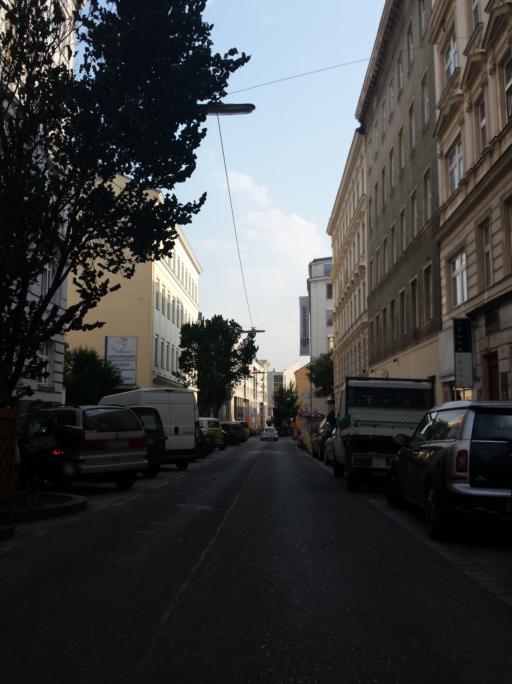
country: AT
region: Vienna
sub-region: Wien Stadt
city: Vienna
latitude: 48.1985
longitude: 16.3969
